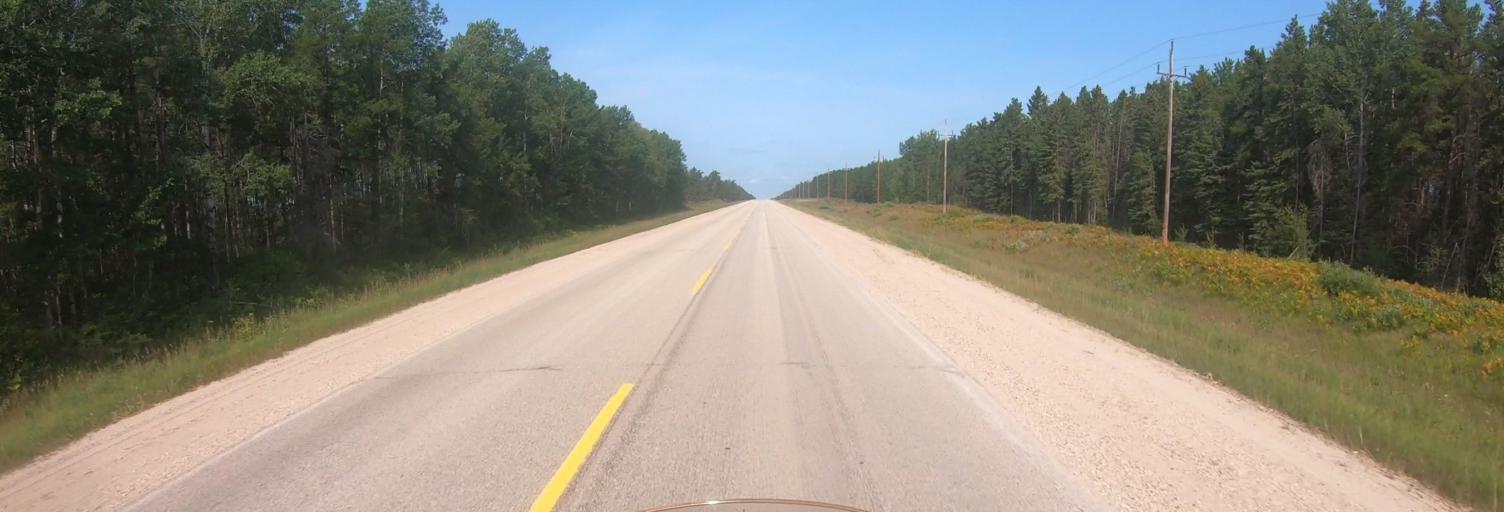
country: US
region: Minnesota
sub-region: Roseau County
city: Roseau
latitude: 49.1195
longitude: -96.0532
